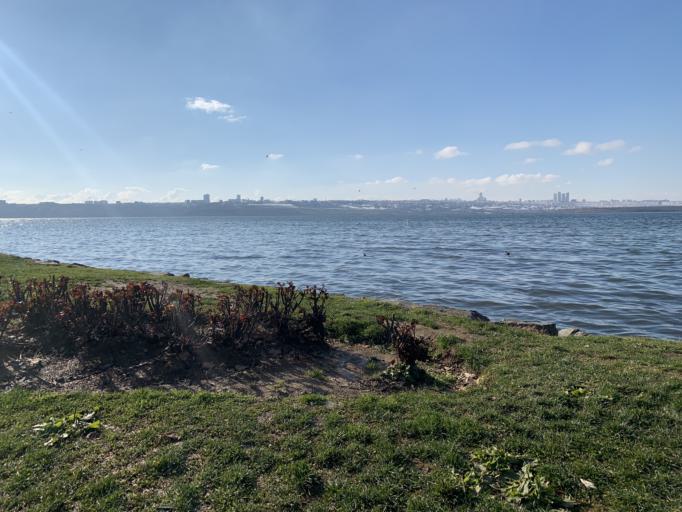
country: TR
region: Istanbul
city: Mahmutbey
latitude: 41.0035
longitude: 28.7697
